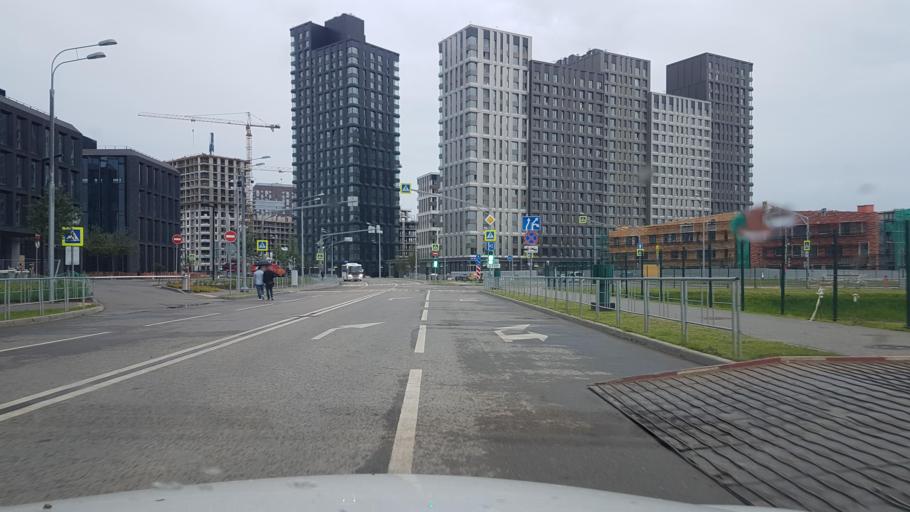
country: RU
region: Moscow
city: Strogino
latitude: 55.8225
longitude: 37.4240
